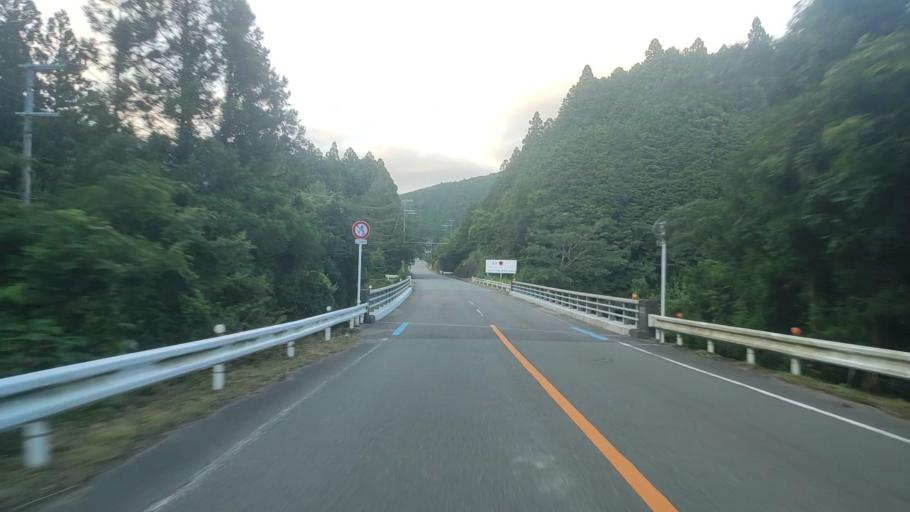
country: JP
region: Wakayama
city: Tanabe
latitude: 33.8199
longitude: 135.6260
